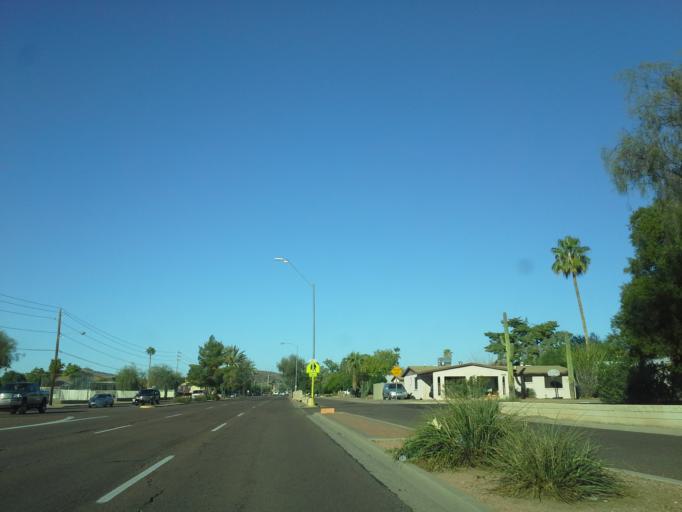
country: US
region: Arizona
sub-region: Maricopa County
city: Paradise Valley
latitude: 33.5969
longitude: -112.0273
